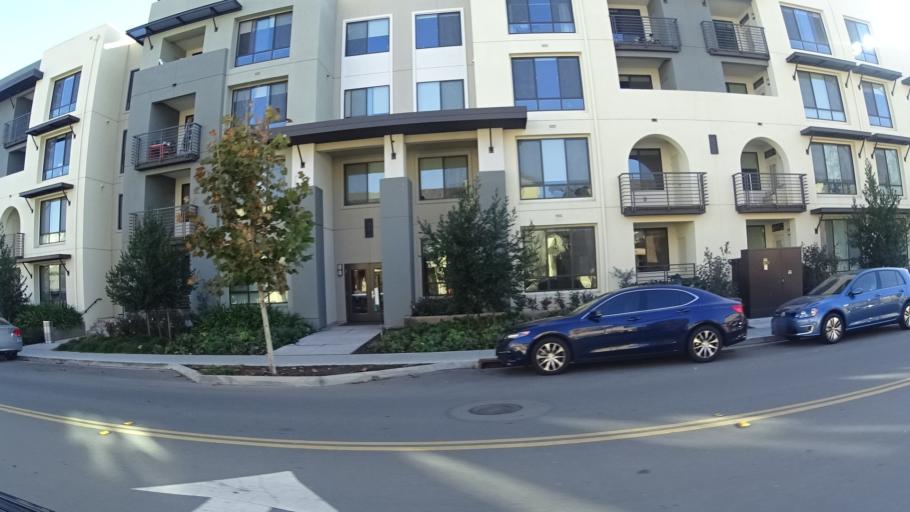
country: US
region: California
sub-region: Santa Clara County
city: Santa Clara
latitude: 37.3419
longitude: -121.9795
